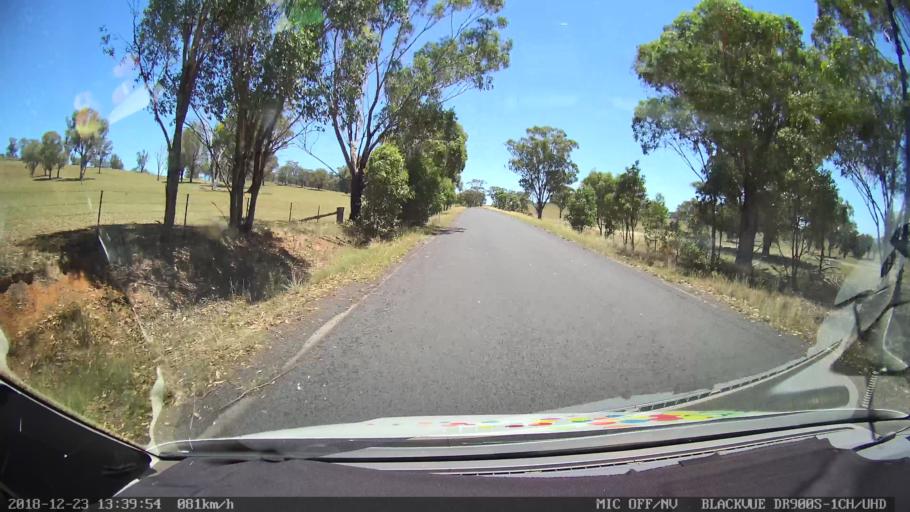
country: AU
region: New South Wales
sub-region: Armidale Dumaresq
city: Armidale
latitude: -30.4622
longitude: 151.1968
